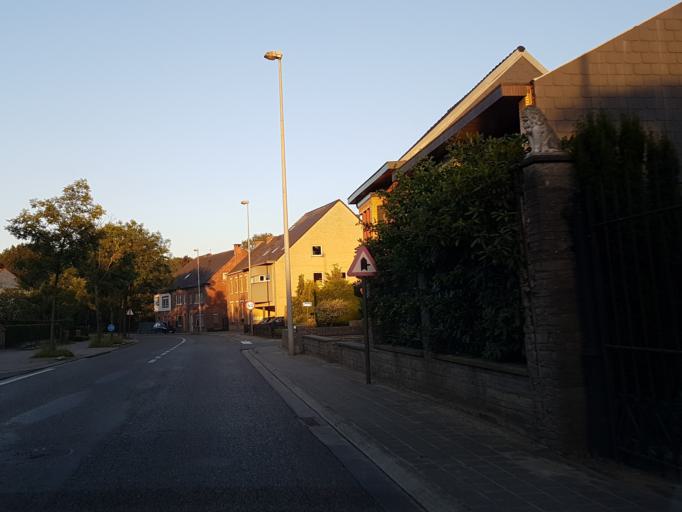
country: BE
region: Flanders
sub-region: Provincie Oost-Vlaanderen
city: Hamme
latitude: 51.1143
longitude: 4.1645
